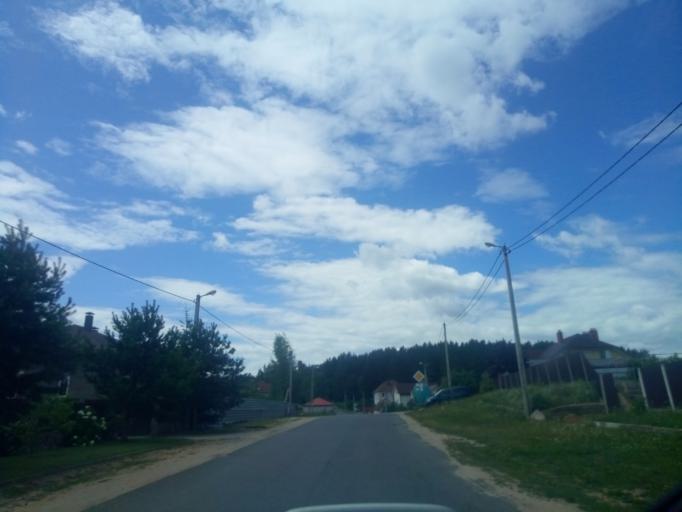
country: BY
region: Minsk
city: Zhdanovichy
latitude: 53.9473
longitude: 27.4103
